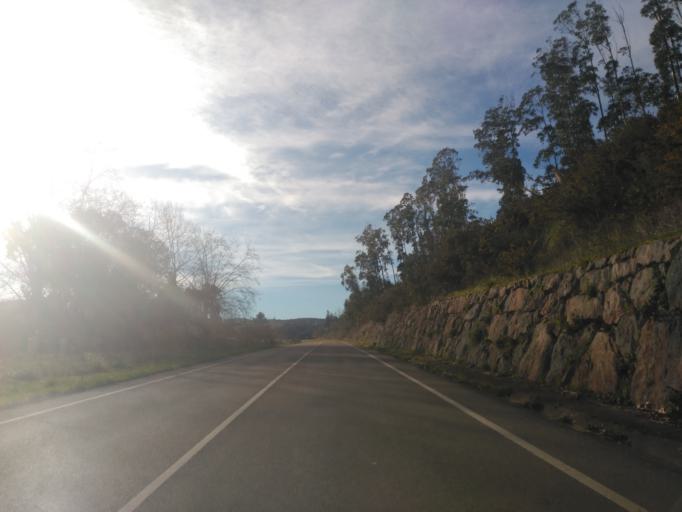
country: ES
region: Cantabria
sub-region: Provincia de Cantabria
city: Comillas
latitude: 43.3675
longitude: -4.2772
